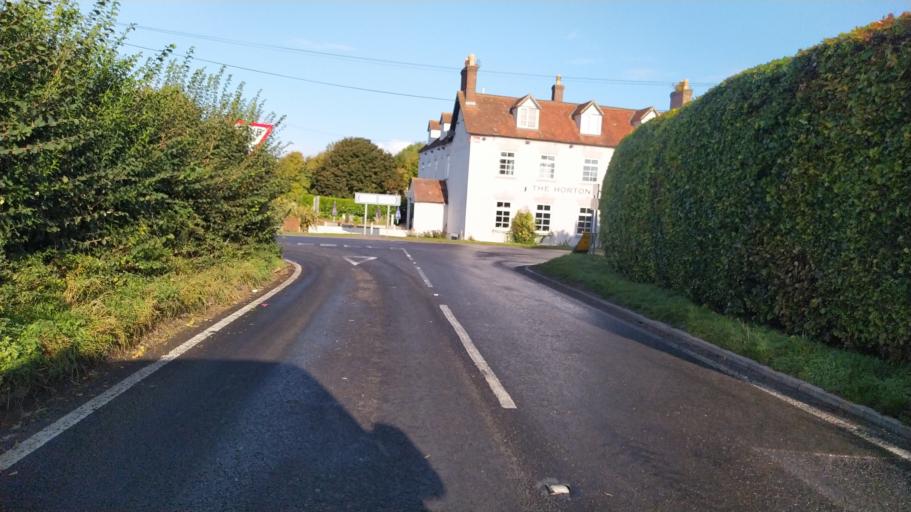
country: GB
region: England
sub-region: Dorset
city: Wimborne Minster
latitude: 50.8768
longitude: -1.9767
